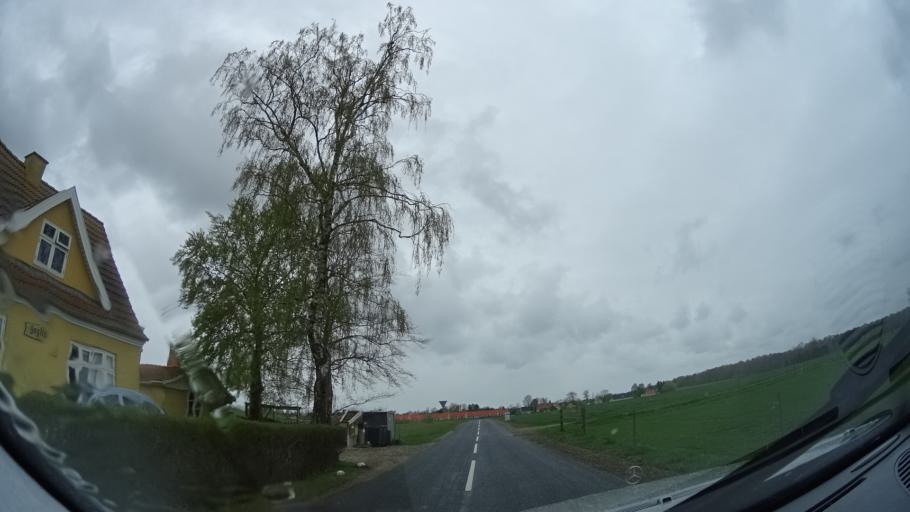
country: DK
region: Zealand
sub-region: Holbaek Kommune
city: Vipperod
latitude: 55.7007
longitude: 11.7796
